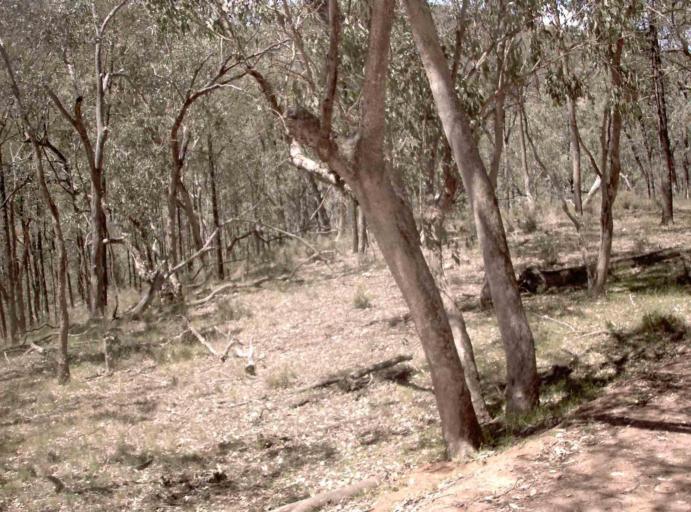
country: AU
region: New South Wales
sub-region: Snowy River
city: Jindabyne
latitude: -37.0896
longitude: 148.4324
